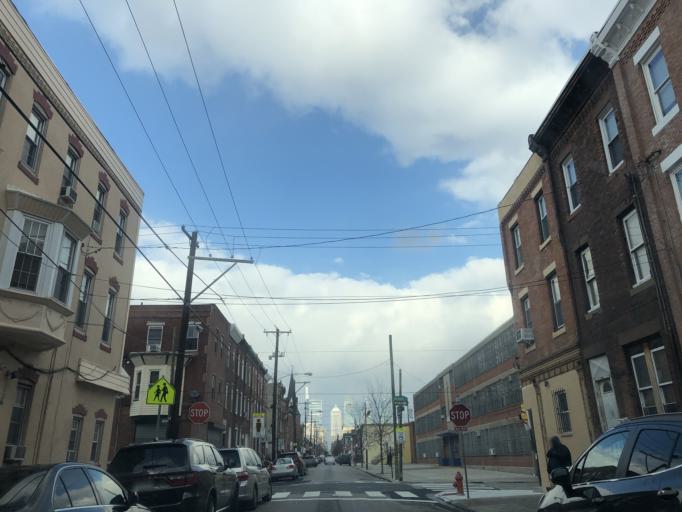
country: US
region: Pennsylvania
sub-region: Philadelphia County
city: Philadelphia
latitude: 39.9298
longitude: -75.1751
